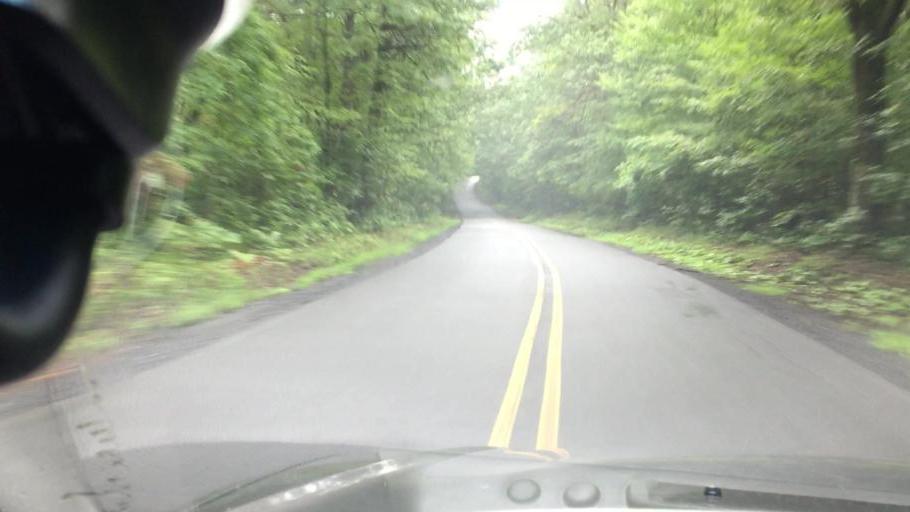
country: US
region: Pennsylvania
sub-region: Luzerne County
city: Freeland
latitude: 41.0223
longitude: -75.9126
